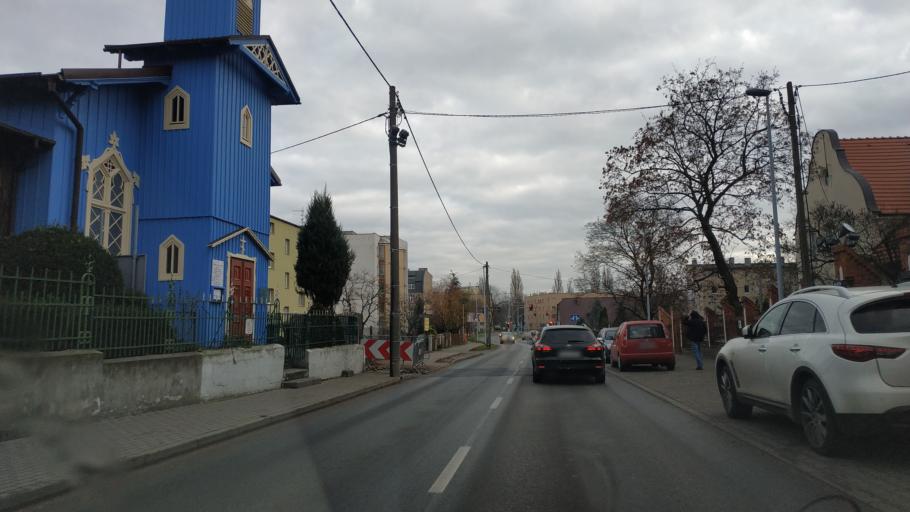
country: PL
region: Kujawsko-Pomorskie
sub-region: Torun
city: Torun
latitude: 53.0226
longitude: 18.6096
